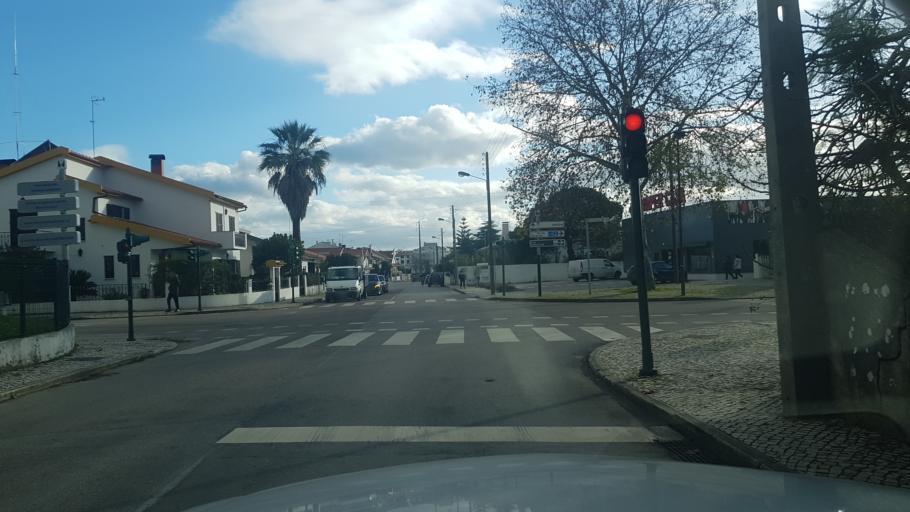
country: PT
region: Santarem
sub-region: Entroncamento
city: Entroncamento
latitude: 39.4741
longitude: -8.4732
